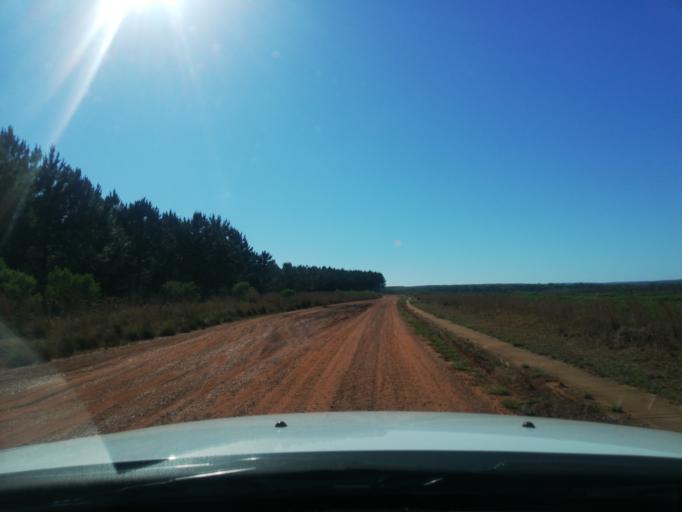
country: AR
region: Misiones
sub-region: Departamento de Candelaria
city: Candelaria
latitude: -27.4914
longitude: -55.7778
